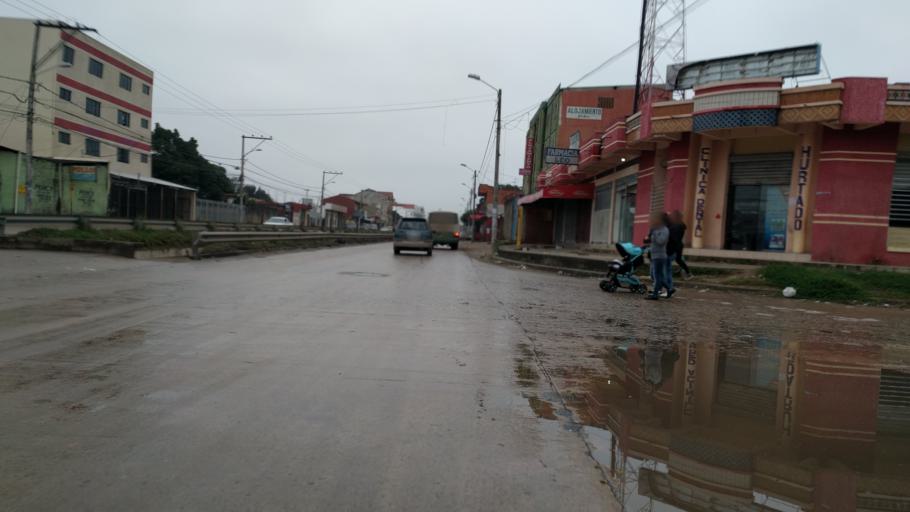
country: BO
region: Santa Cruz
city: Santa Cruz de la Sierra
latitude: -17.8276
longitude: -63.1704
